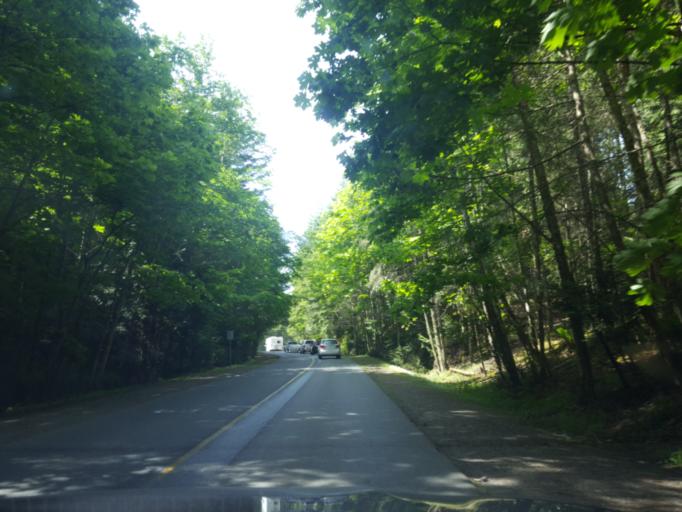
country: CA
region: British Columbia
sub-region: Regional District of Nanaimo
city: Parksville
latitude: 49.3156
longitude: -124.2743
